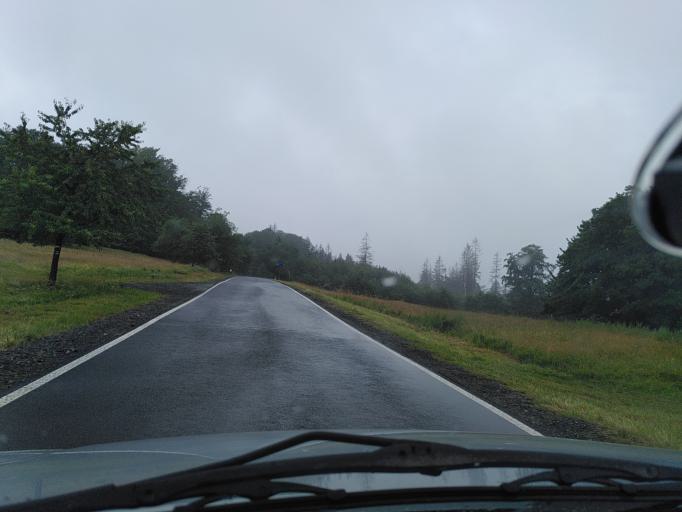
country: CZ
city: Novy Bor
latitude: 50.7846
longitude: 14.5209
